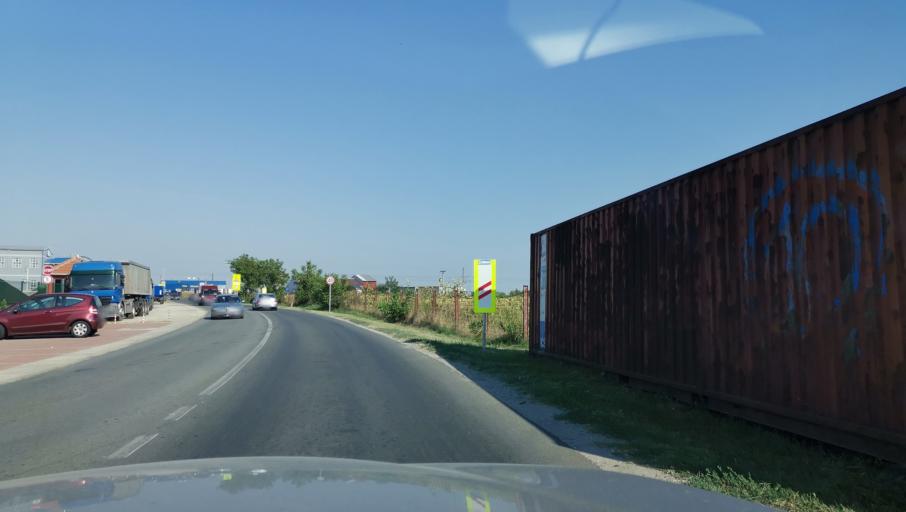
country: RS
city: Dobanovci
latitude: 44.8109
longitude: 20.2438
